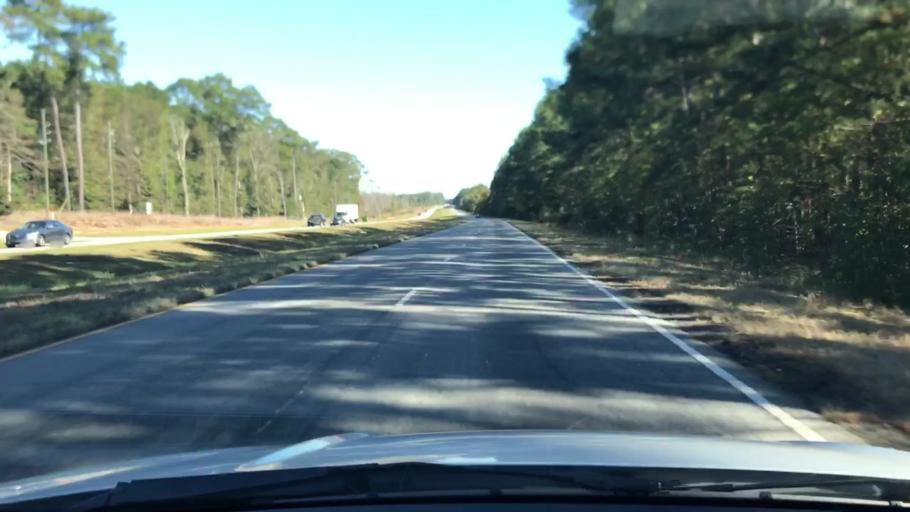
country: US
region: South Carolina
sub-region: Charleston County
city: Ravenel
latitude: 32.7574
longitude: -80.3776
